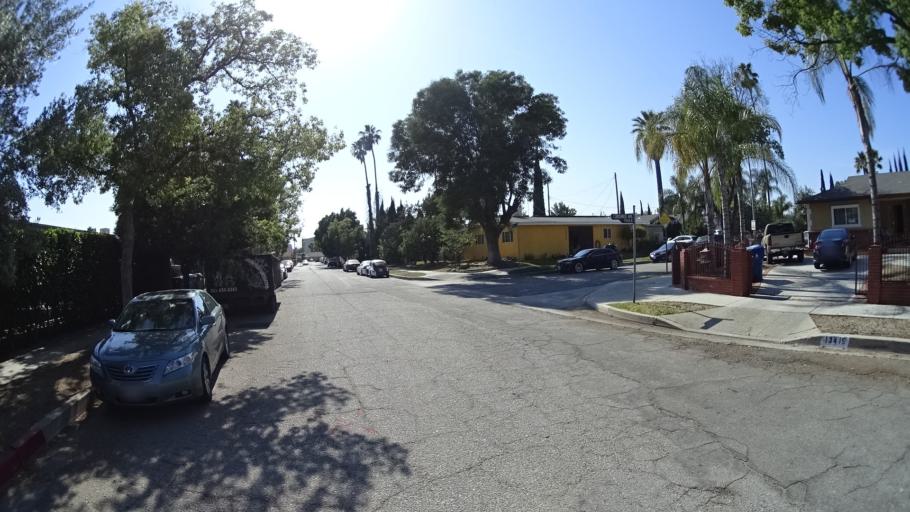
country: US
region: California
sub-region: Los Angeles County
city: Van Nuys
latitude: 34.2149
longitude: -118.4255
